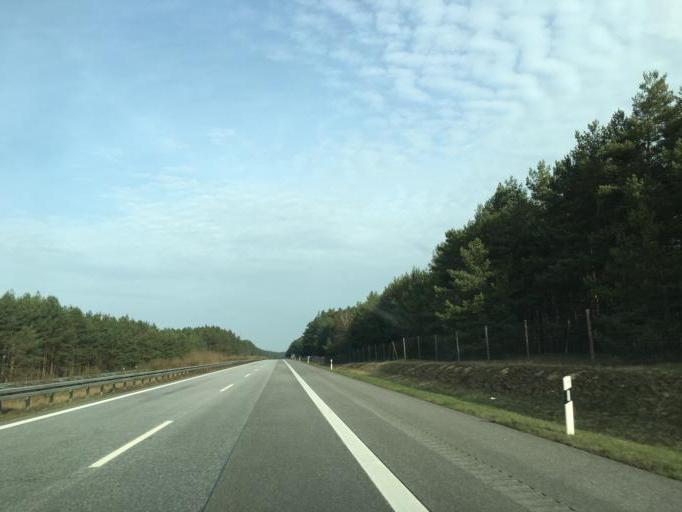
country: DE
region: Mecklenburg-Vorpommern
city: Malchow
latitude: 53.5413
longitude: 12.3402
